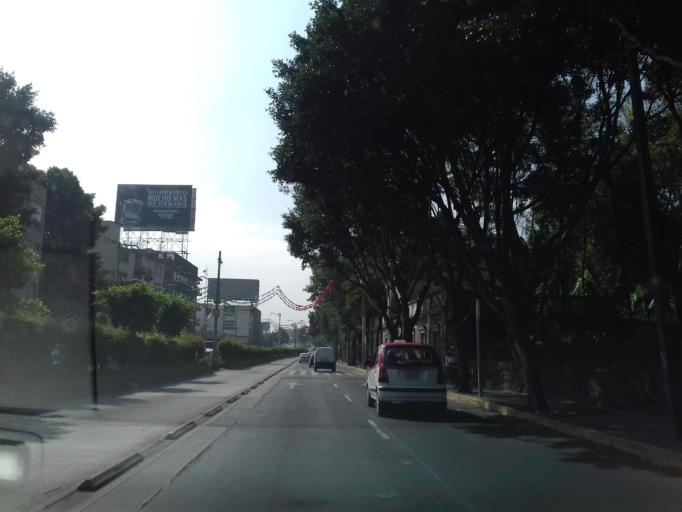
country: MX
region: Mexico City
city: Polanco
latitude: 19.4061
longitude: -99.1888
